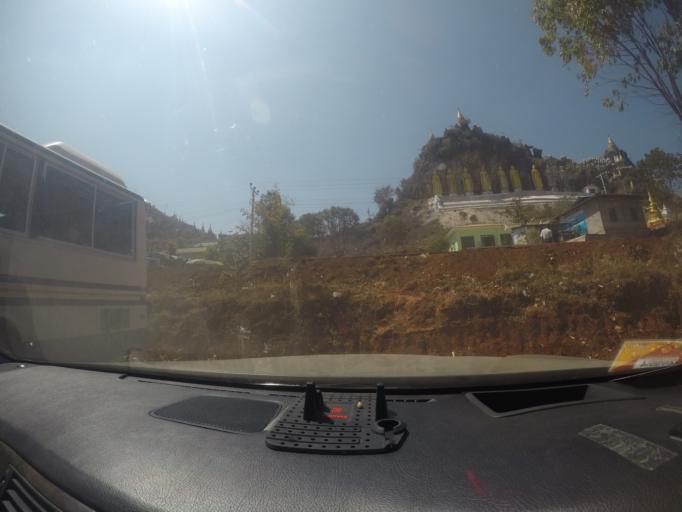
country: MM
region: Shan
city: Taunggyi
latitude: 20.9157
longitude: 96.5607
